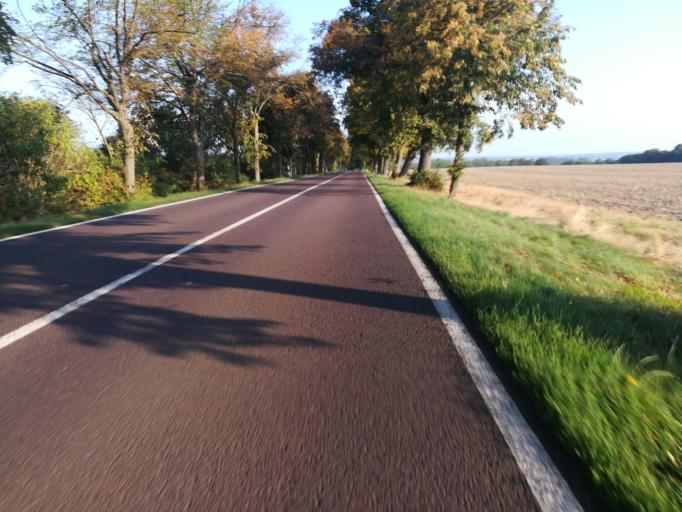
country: DE
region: Saxony-Anhalt
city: Haldensleben I
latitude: 52.2499
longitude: 11.4338
